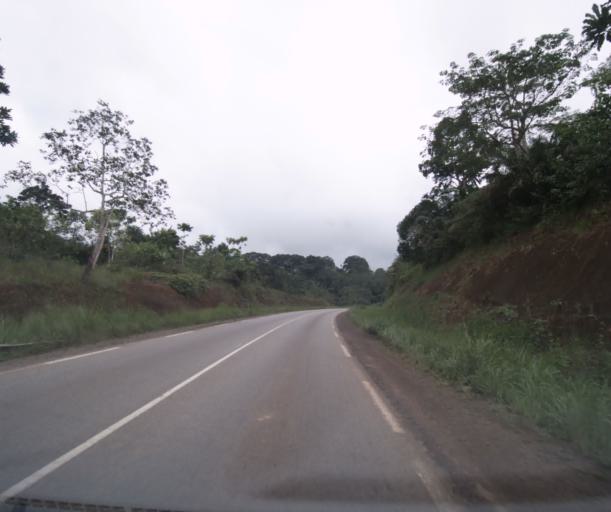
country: CM
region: Littoral
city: Edea
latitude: 3.8145
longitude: 10.3304
